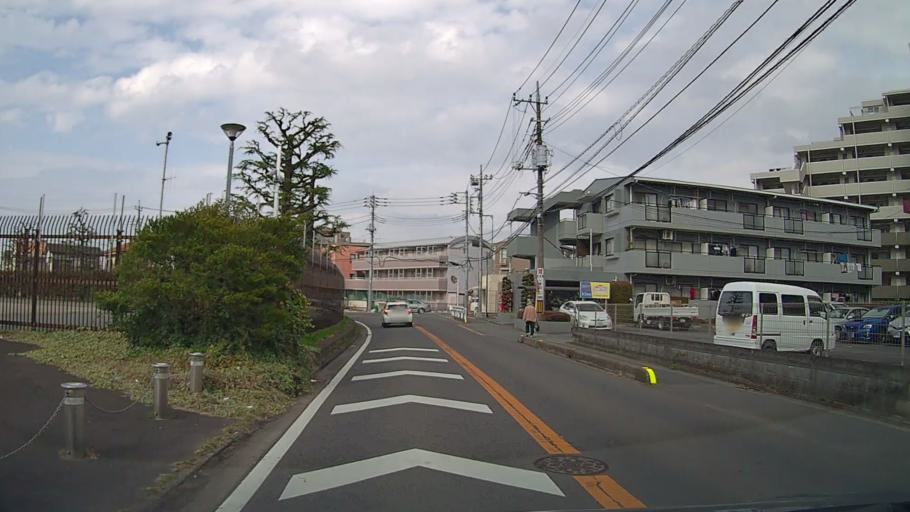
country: JP
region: Saitama
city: Shiki
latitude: 35.8215
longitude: 139.5945
